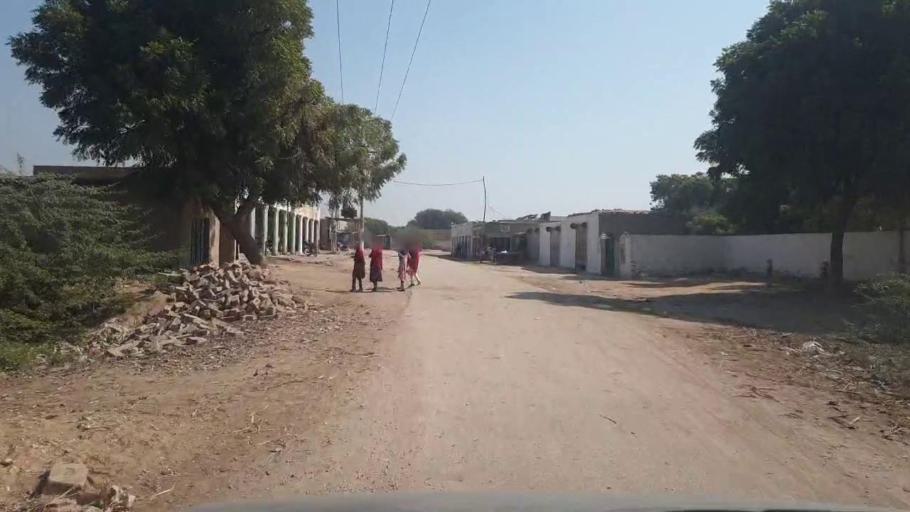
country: PK
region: Sindh
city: Chambar
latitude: 25.2614
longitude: 68.8295
